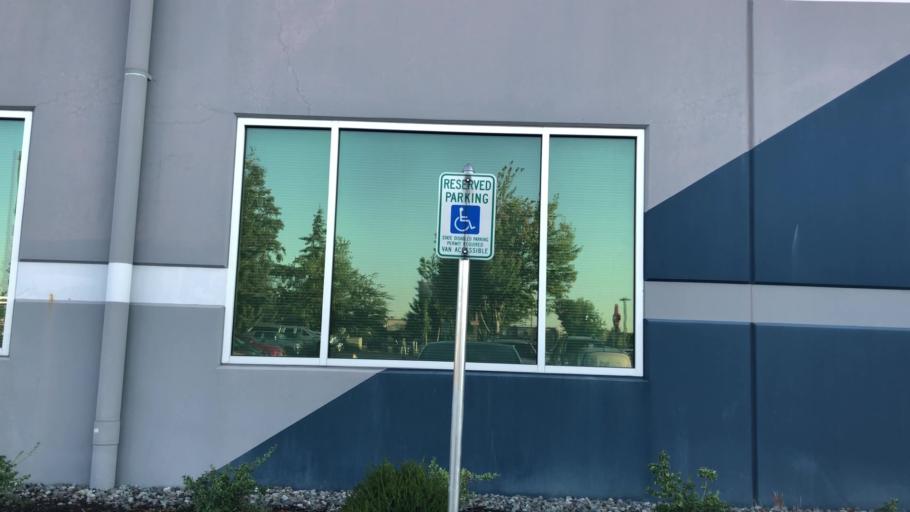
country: US
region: Washington
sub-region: King County
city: Auburn
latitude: 47.3221
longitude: -122.2284
